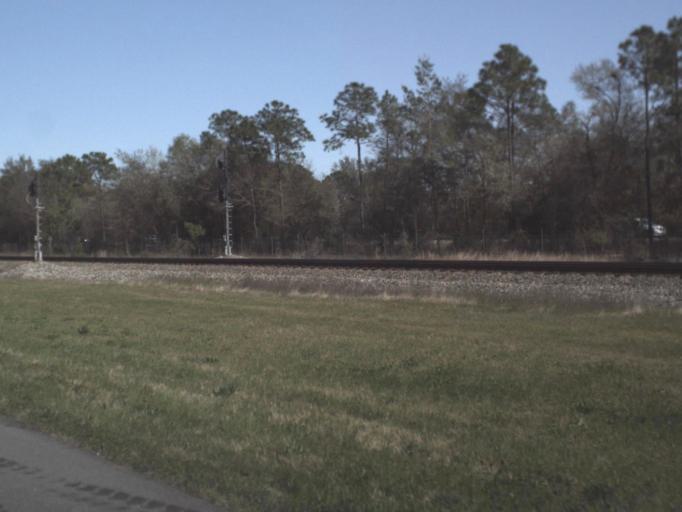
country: US
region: Florida
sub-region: Walton County
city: DeFuniak Springs
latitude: 30.7467
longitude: -86.3014
